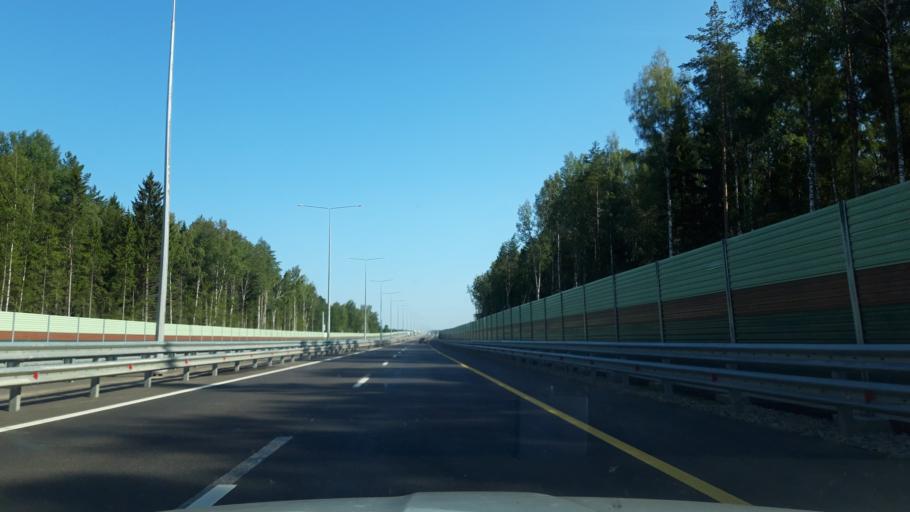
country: RU
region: Moskovskaya
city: Reshetnikovo
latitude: 56.4515
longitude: 36.5411
